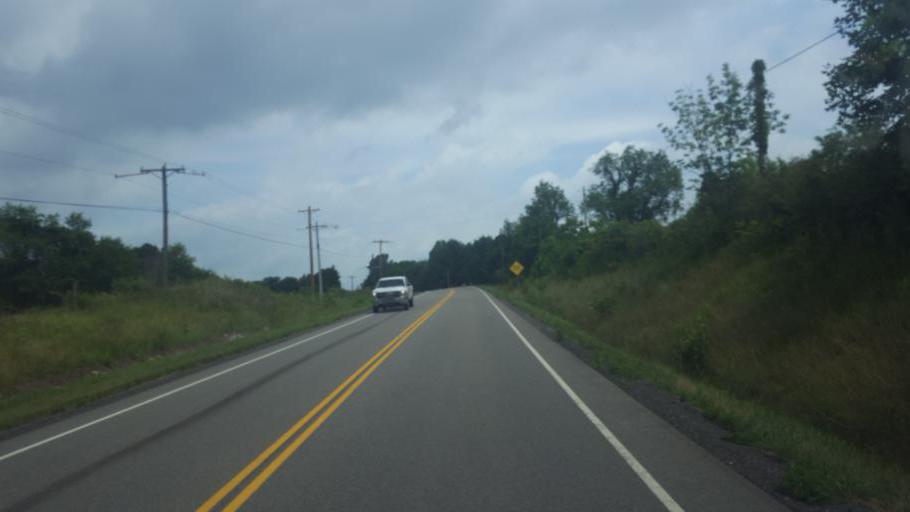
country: US
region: Ohio
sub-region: Licking County
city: Utica
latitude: 40.1809
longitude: -82.5187
